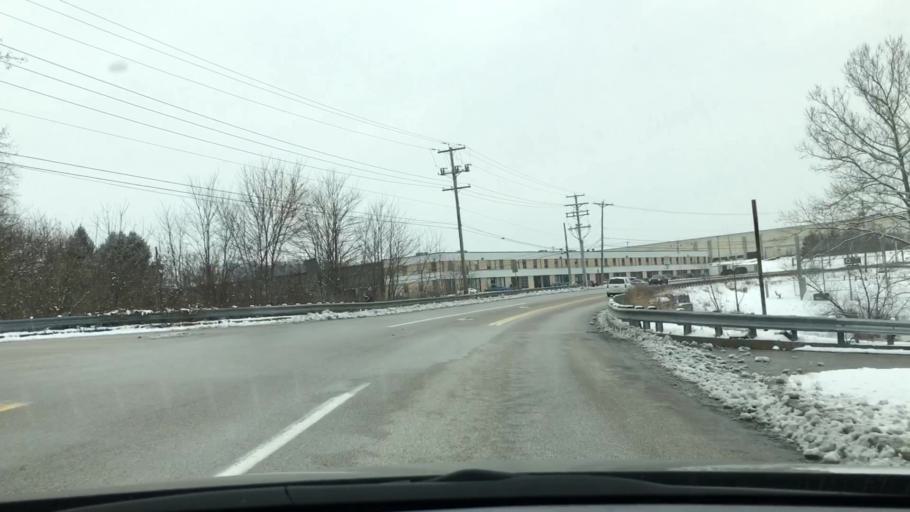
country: US
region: Pennsylvania
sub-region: York County
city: Emigsville
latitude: 40.0107
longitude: -76.7147
